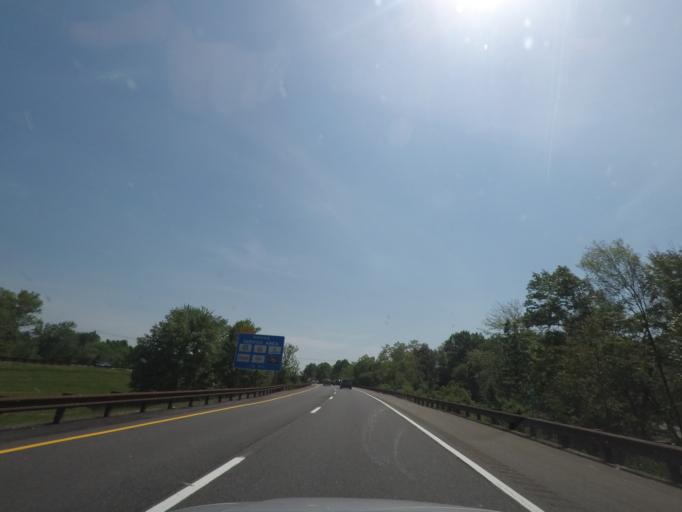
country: US
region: New York
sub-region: Rockland County
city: Chestnut Ridge
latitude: 41.0596
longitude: -74.0652
